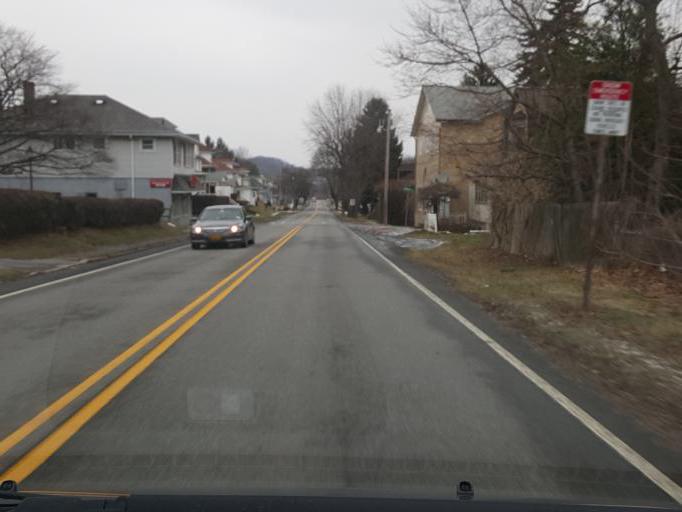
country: US
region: Pennsylvania
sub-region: Blair County
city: Altoona
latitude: 40.5234
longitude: -78.3757
